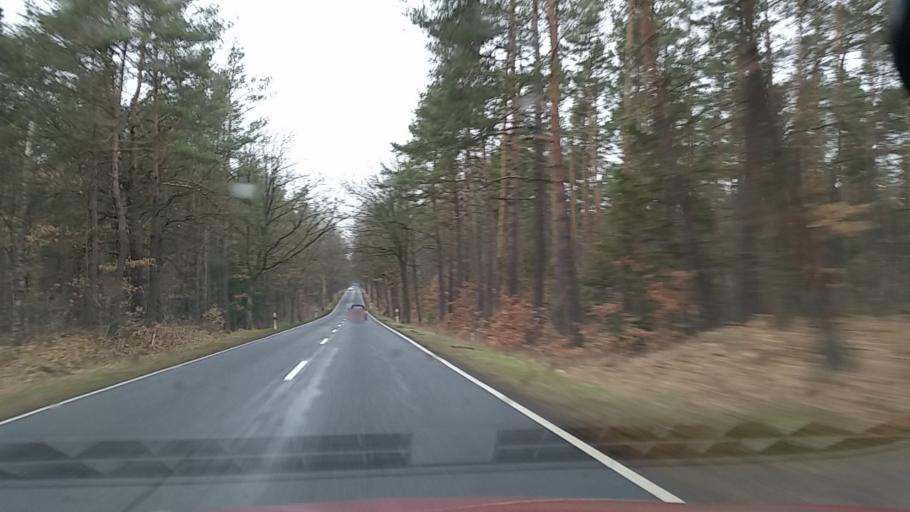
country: DE
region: Lower Saxony
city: Sprakensehl
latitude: 52.7734
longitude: 10.4471
